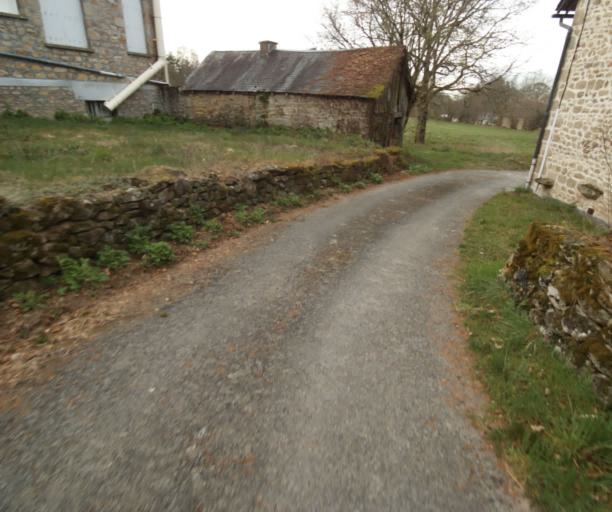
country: FR
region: Limousin
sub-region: Departement de la Correze
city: Correze
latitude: 45.4237
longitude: 1.8378
